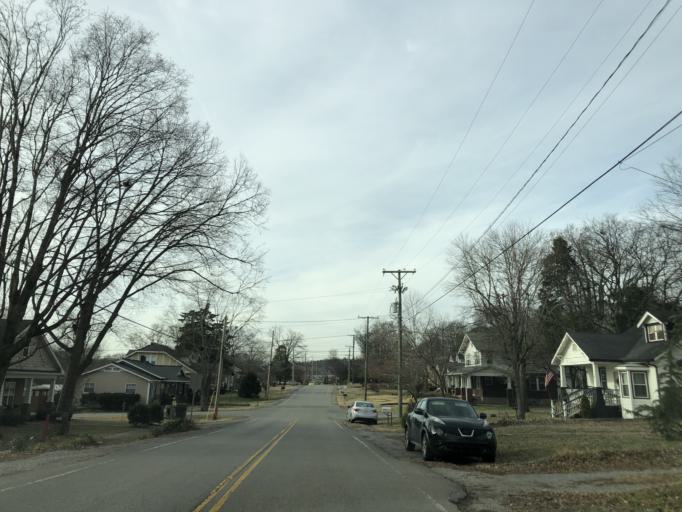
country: US
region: Tennessee
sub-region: Davidson County
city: Nashville
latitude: 36.2091
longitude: -86.7281
